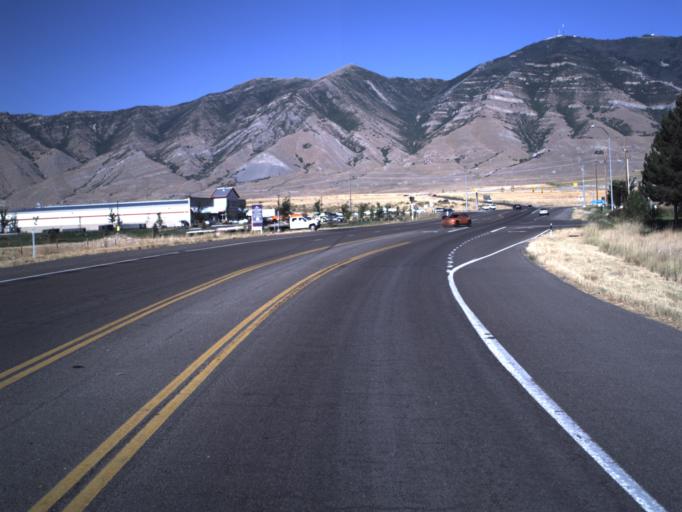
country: US
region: Utah
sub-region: Tooele County
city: Stansbury park
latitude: 40.6529
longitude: -112.2927
